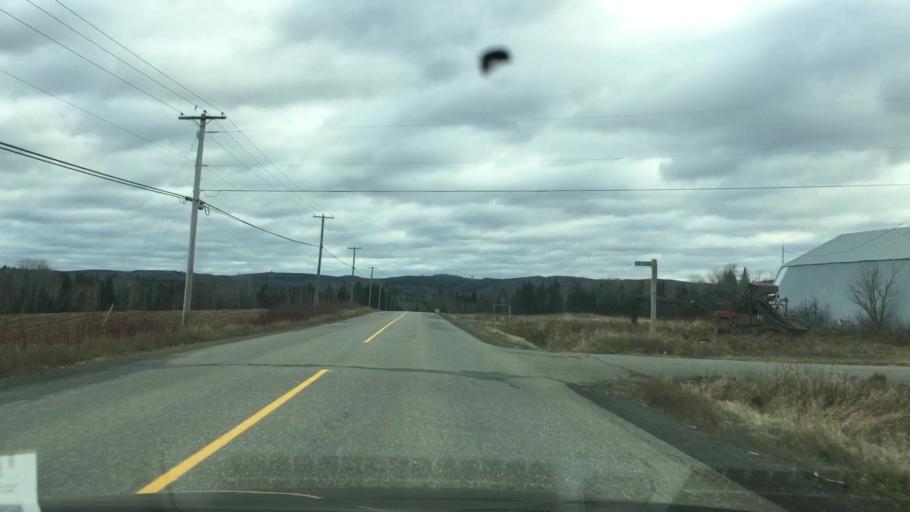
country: US
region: Maine
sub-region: Aroostook County
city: Fort Fairfield
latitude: 46.7497
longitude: -67.7364
